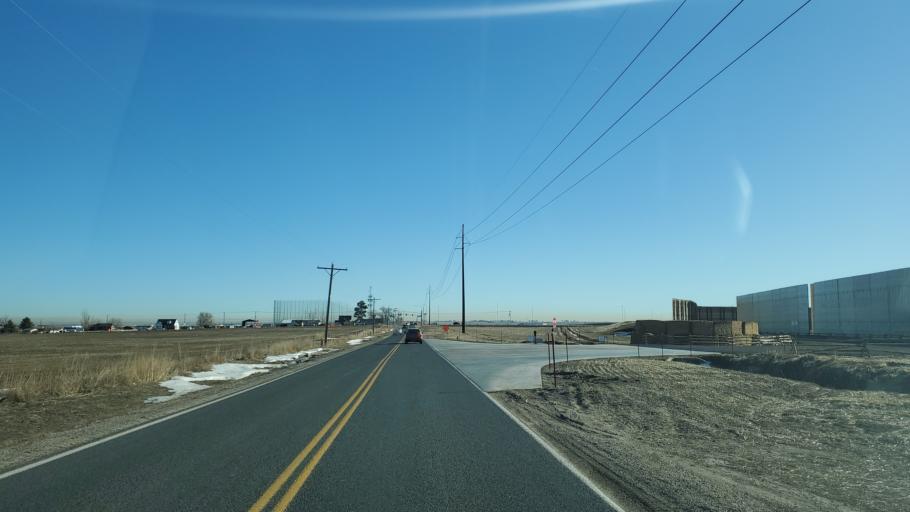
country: US
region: Colorado
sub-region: Boulder County
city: Erie
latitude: 39.9865
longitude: -105.0022
